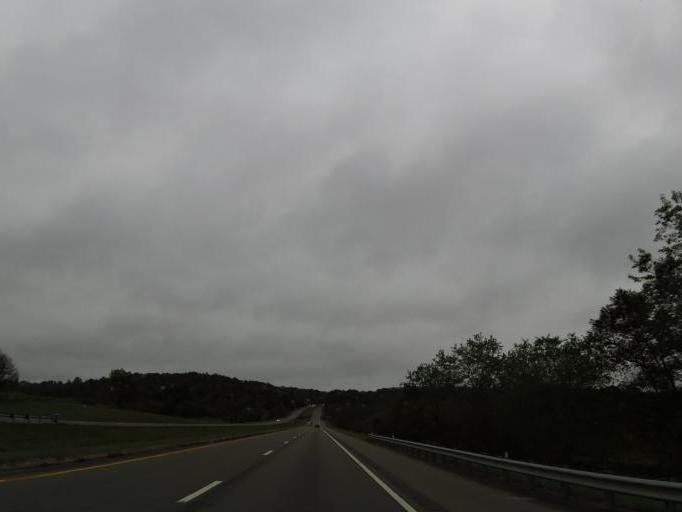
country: US
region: Virginia
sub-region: Wythe County
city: Wytheville
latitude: 36.9867
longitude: -81.0750
